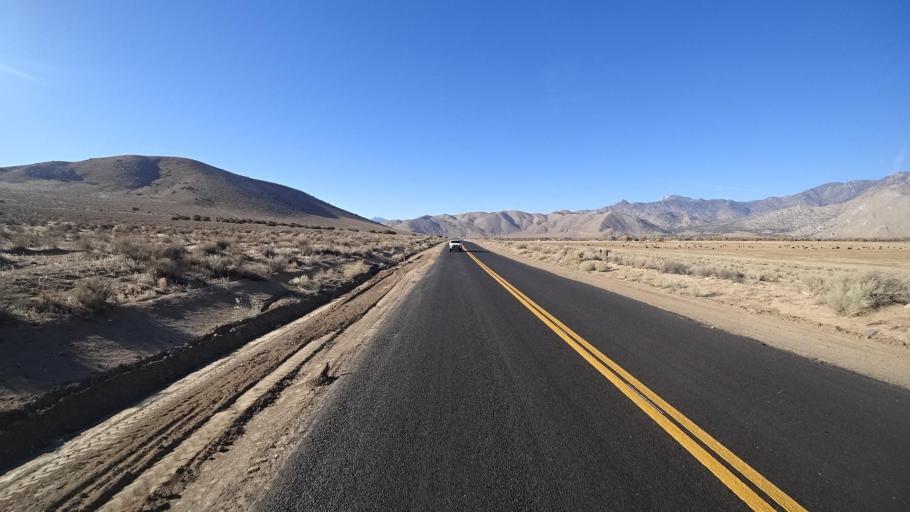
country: US
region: California
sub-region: Kern County
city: Weldon
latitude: 35.6545
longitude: -118.2845
